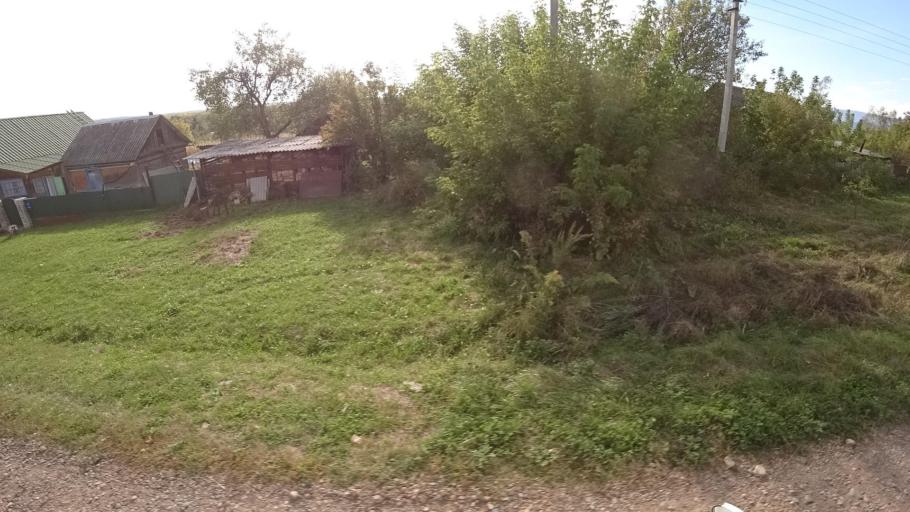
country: RU
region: Primorskiy
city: Dostoyevka
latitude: 44.2953
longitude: 133.4483
